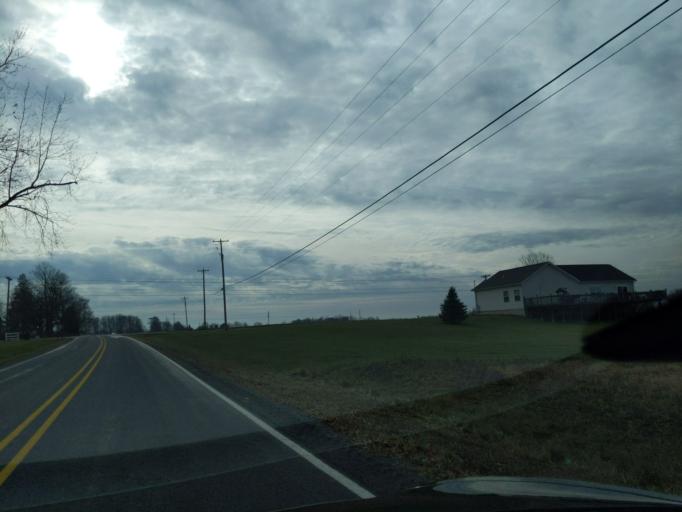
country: US
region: Michigan
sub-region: Ingham County
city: Mason
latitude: 42.5105
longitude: -84.5222
